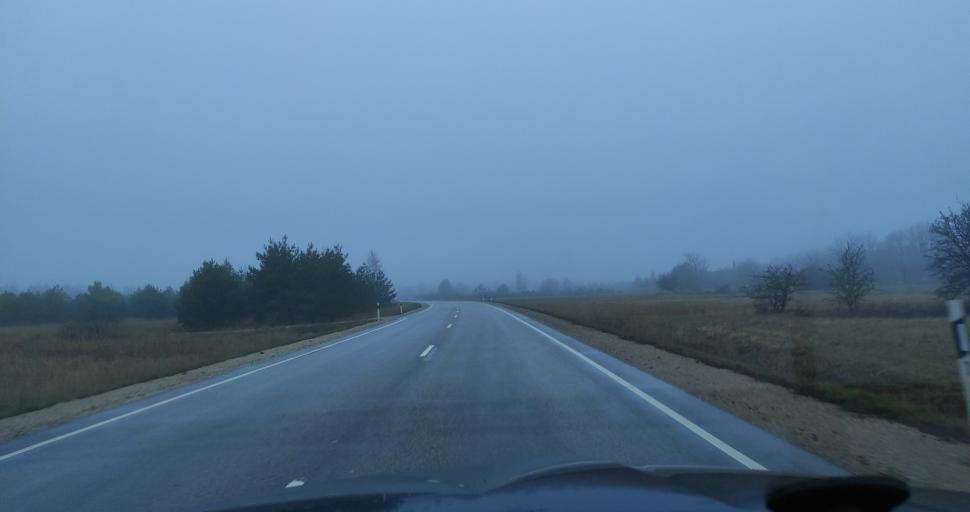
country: LV
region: Pavilostas
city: Pavilosta
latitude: 56.9307
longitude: 21.2712
